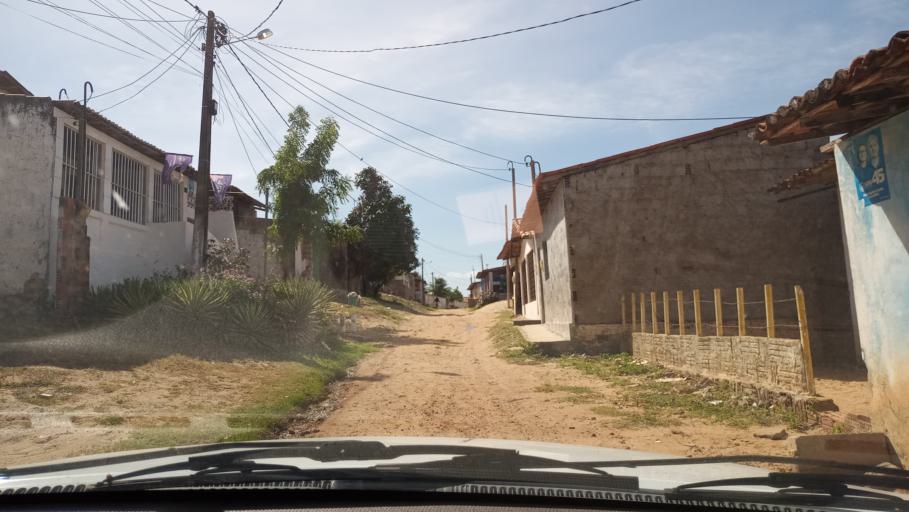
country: BR
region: Rio Grande do Norte
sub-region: Maxaranguape
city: Sao Miguel
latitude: -5.5151
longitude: -35.2640
